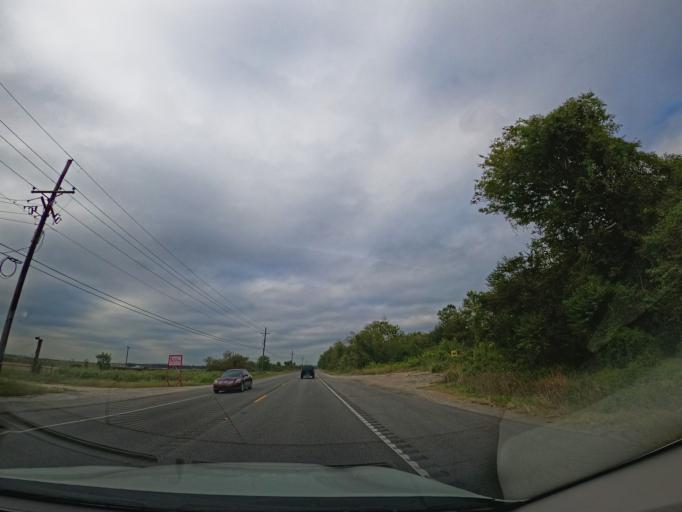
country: US
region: Louisiana
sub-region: Saint Mary Parish
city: Amelia
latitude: 29.6679
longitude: -91.0271
